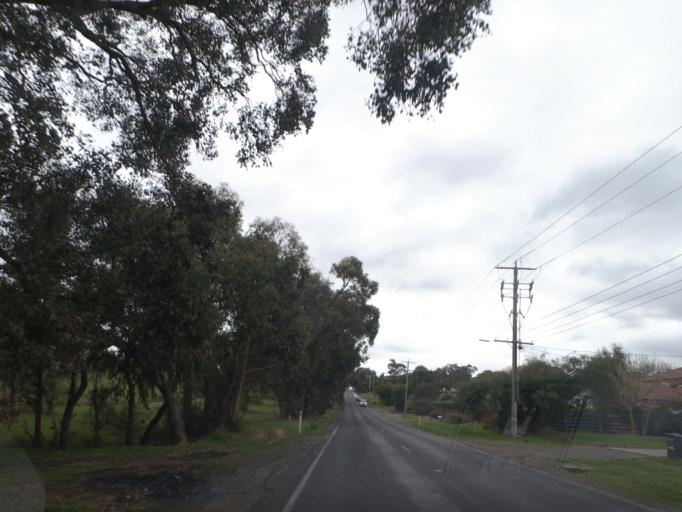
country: AU
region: Victoria
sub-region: Nillumbik
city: Doreen
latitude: -37.6235
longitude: 145.1350
